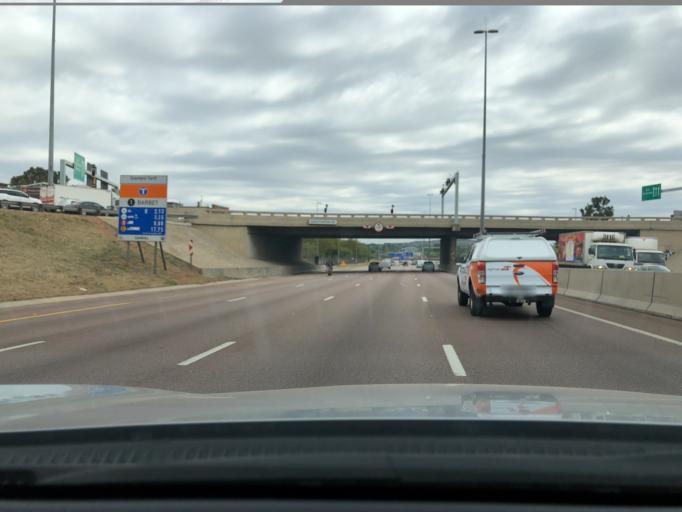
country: ZA
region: Gauteng
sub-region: City of Tshwane Metropolitan Municipality
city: Pretoria
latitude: -25.7859
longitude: 28.2699
